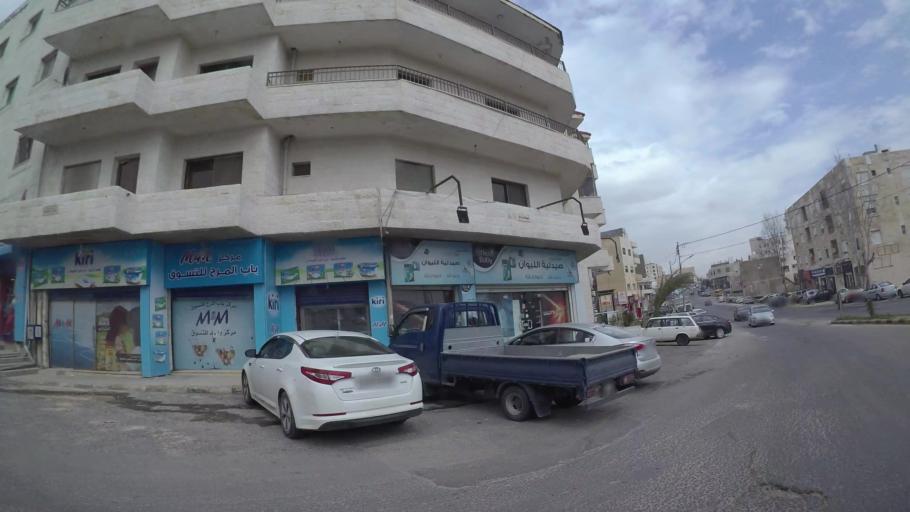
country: JO
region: Amman
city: Umm as Summaq
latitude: 31.9074
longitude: 35.8475
